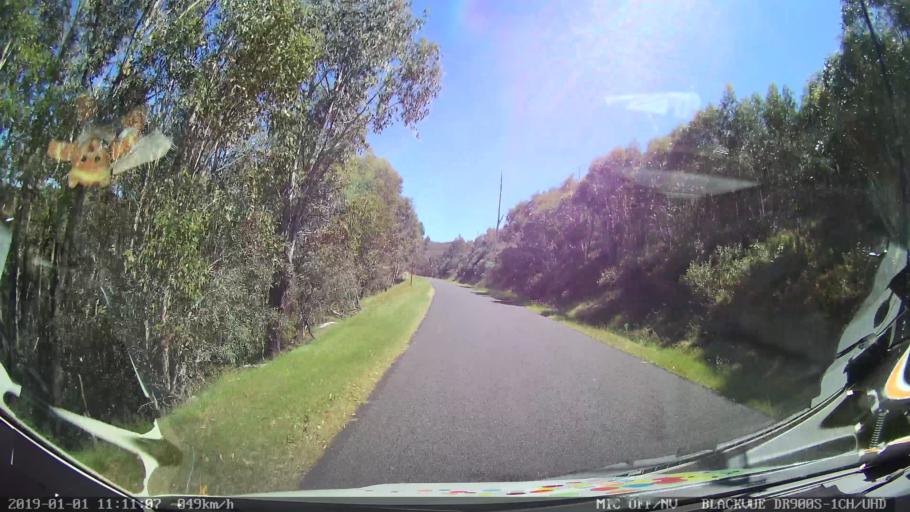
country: AU
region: New South Wales
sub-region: Snowy River
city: Jindabyne
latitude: -35.9643
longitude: 148.4009
